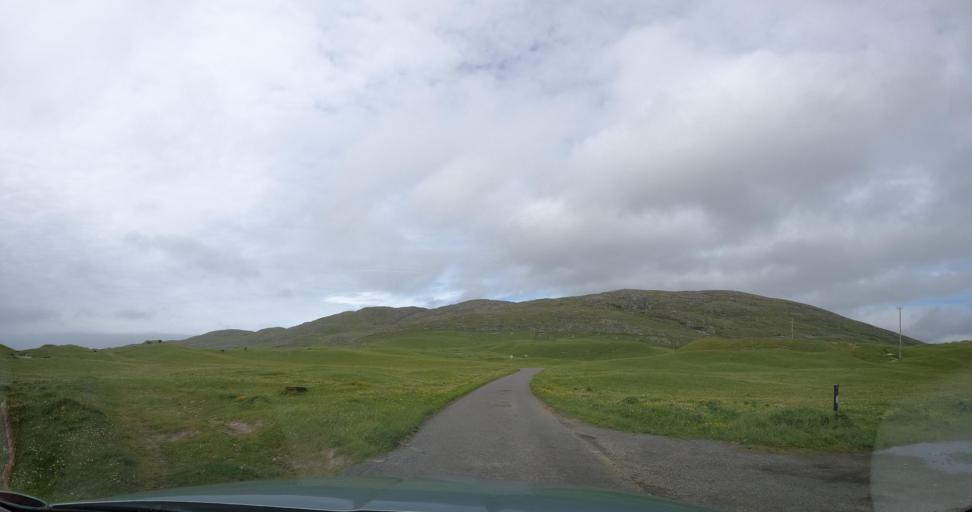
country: GB
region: Scotland
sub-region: Eilean Siar
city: Barra
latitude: 56.9234
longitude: -7.5384
